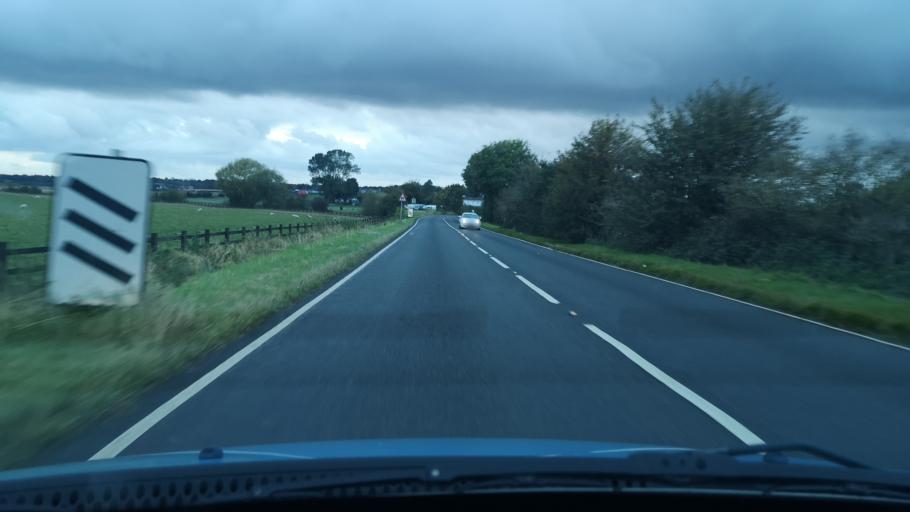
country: GB
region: England
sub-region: City and Borough of Wakefield
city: Badsworth
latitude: 53.6437
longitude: -1.2827
